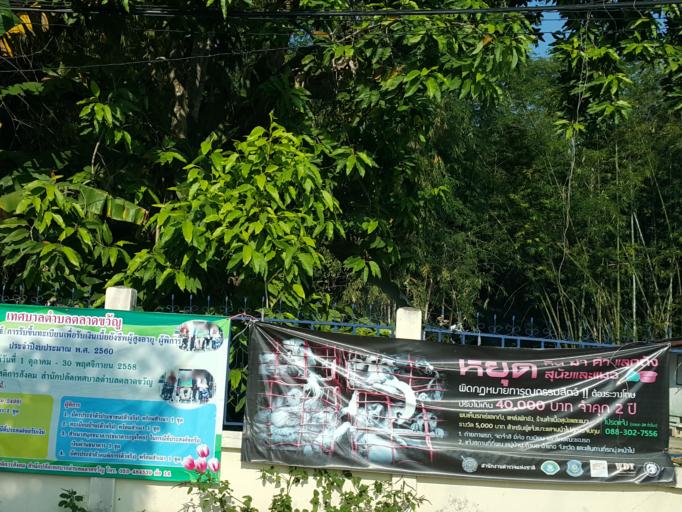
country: TH
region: Chiang Mai
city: San Sai
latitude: 18.8556
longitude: 99.1016
